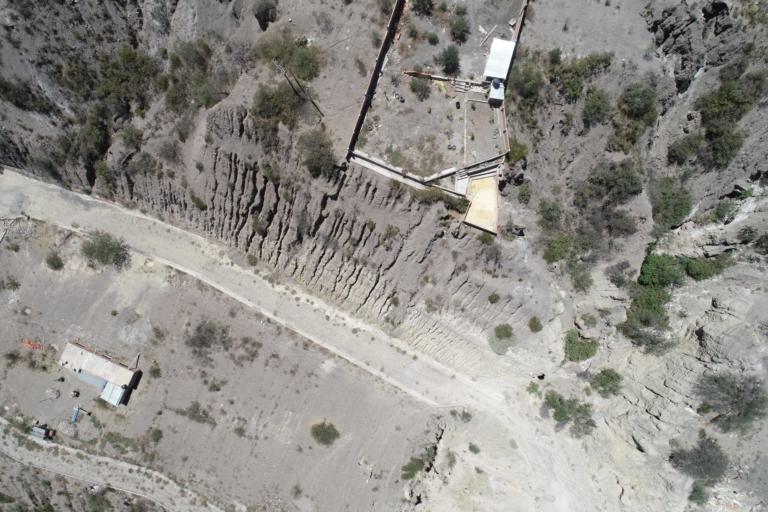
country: BO
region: La Paz
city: La Paz
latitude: -16.6163
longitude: -68.0592
